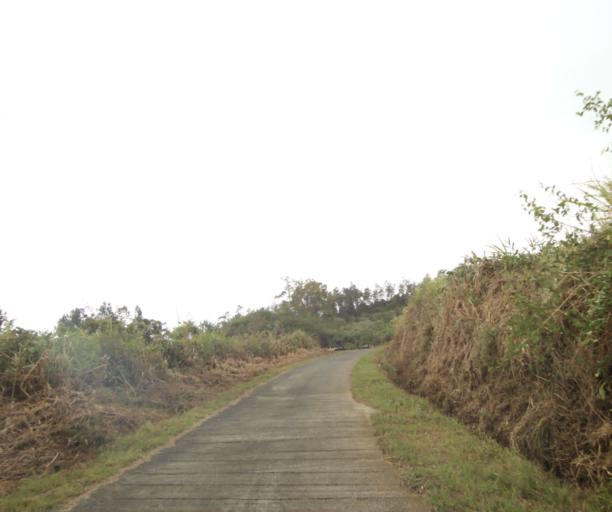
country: RE
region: Reunion
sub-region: Reunion
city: Saint-Paul
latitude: -21.0137
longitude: 55.3470
